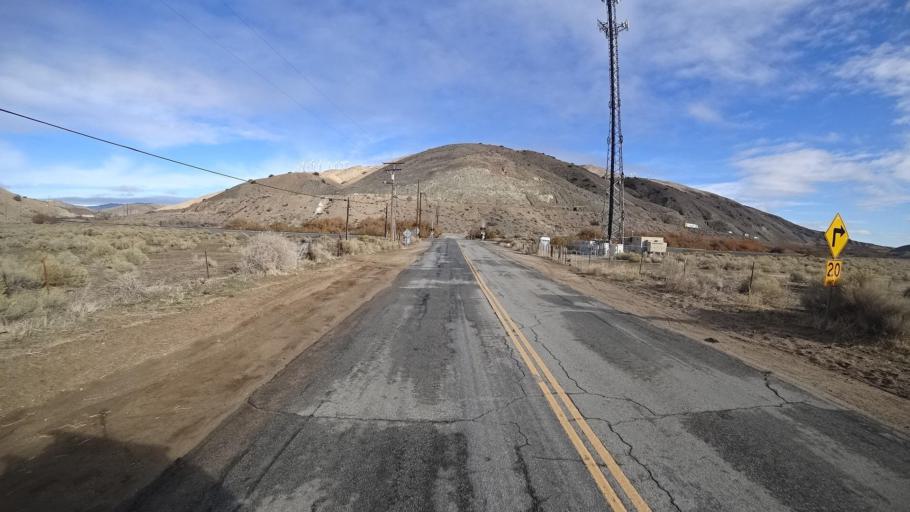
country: US
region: California
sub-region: Kern County
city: Mojave
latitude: 35.0952
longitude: -118.3051
